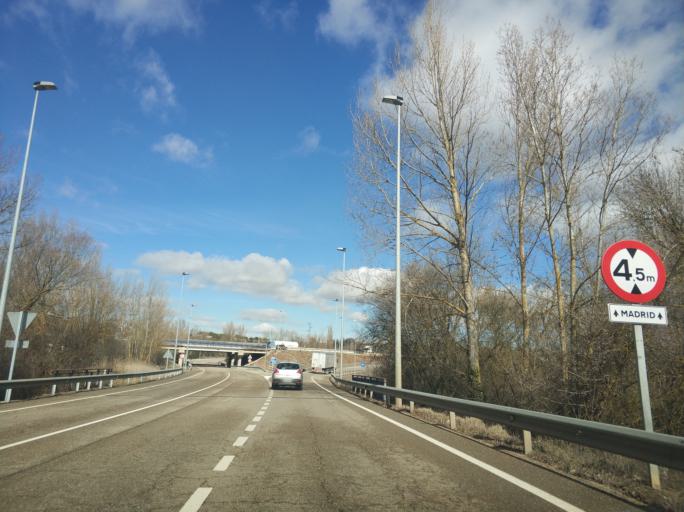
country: ES
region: Castille and Leon
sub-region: Provincia de Burgos
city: Saldana de Burgos
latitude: 42.2624
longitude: -3.6974
